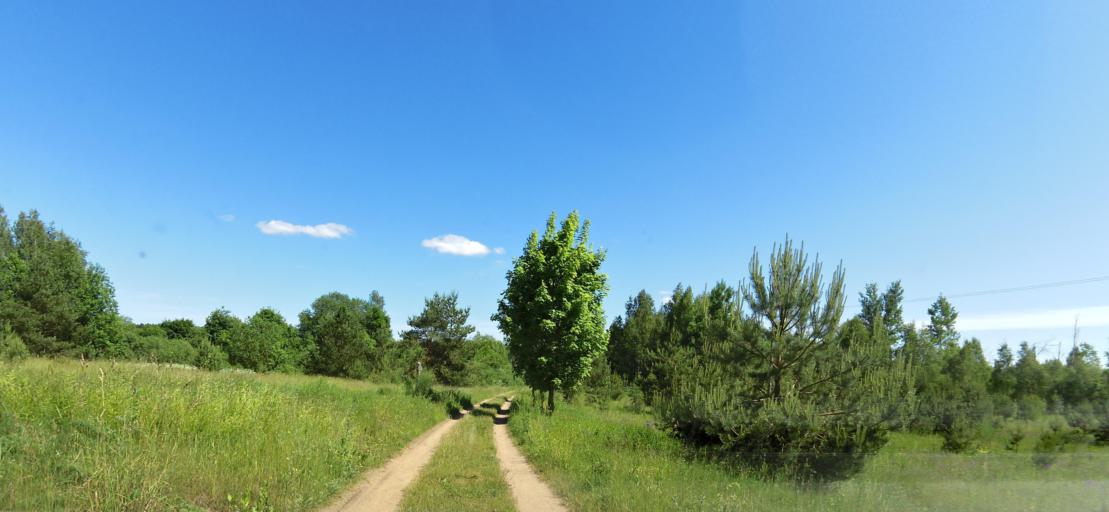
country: LT
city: Sirvintos
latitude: 55.2569
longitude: 25.1014
